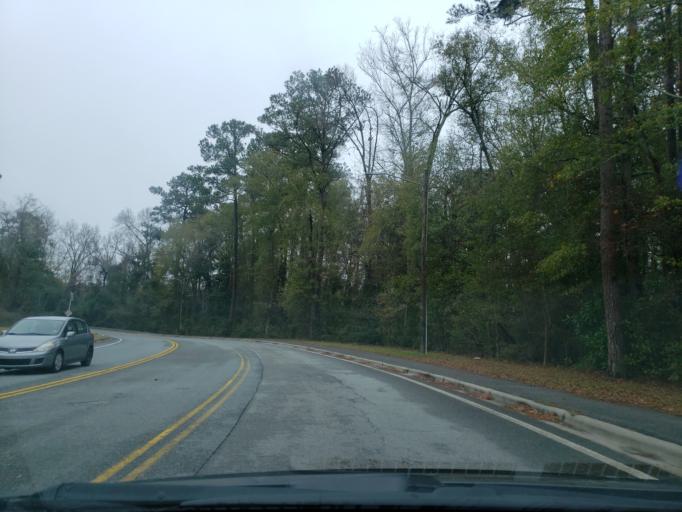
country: US
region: Georgia
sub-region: Chatham County
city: Montgomery
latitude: 31.9749
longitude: -81.1674
